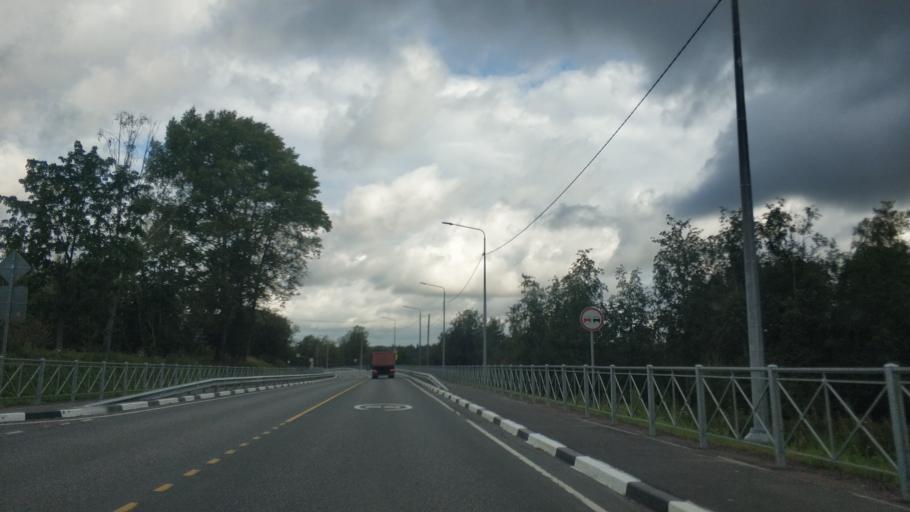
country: RU
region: Republic of Karelia
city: Ruskeala
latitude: 61.9324
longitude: 30.5939
